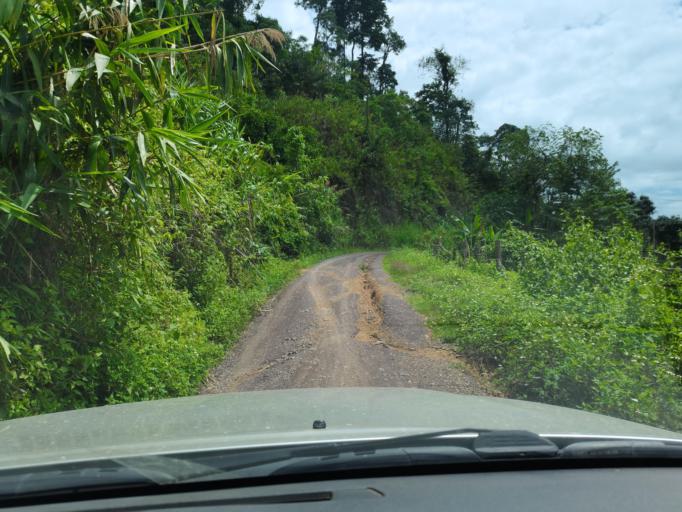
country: LA
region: Loungnamtha
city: Muang Long
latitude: 20.7110
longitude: 101.0122
